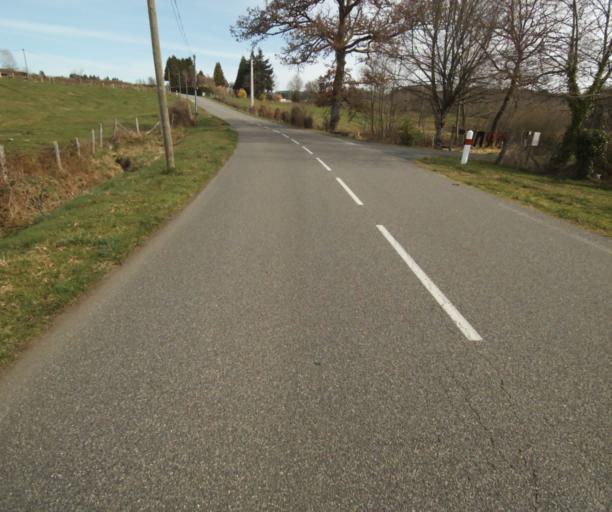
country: FR
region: Limousin
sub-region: Departement de la Correze
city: Correze
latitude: 45.4052
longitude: 1.8266
